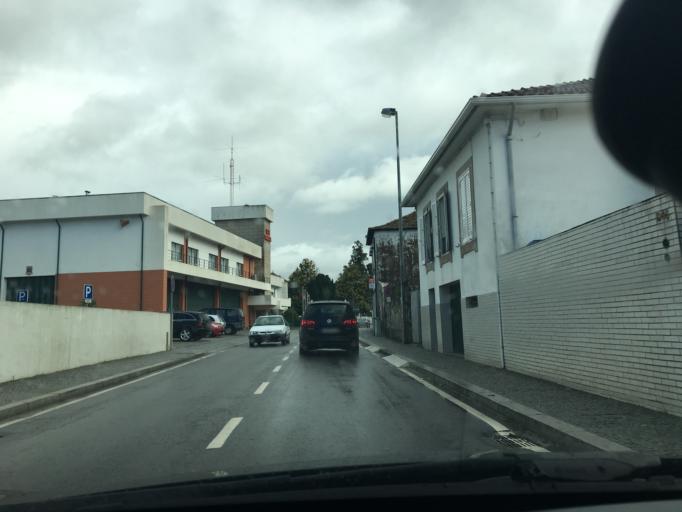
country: PT
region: Porto
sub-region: Maia
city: Gemunde
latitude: 41.2470
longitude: -8.6640
